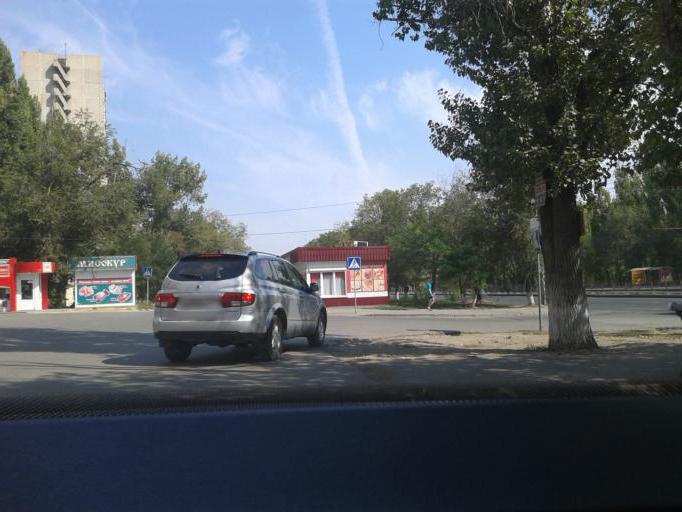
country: RU
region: Volgograd
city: Volgograd
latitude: 48.6208
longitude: 44.4241
